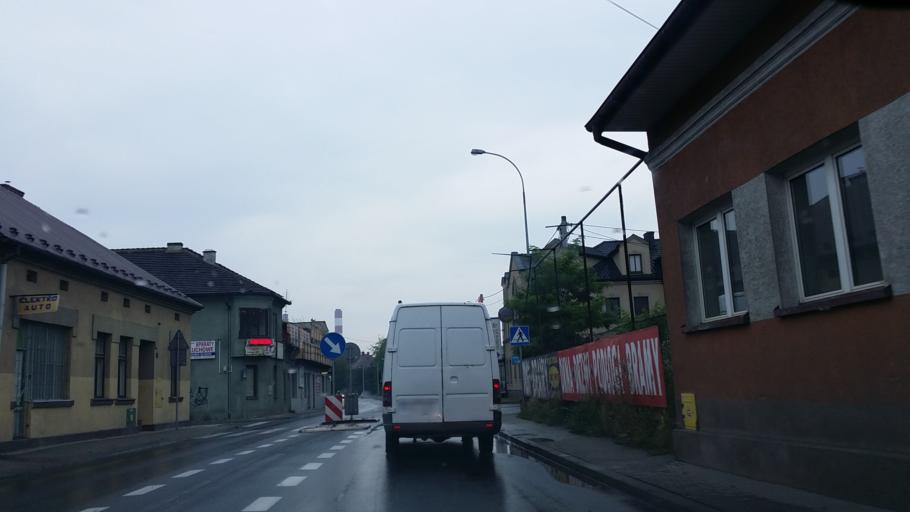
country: PL
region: Lesser Poland Voivodeship
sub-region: Powiat krakowski
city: Skawina
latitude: 49.9757
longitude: 19.8223
